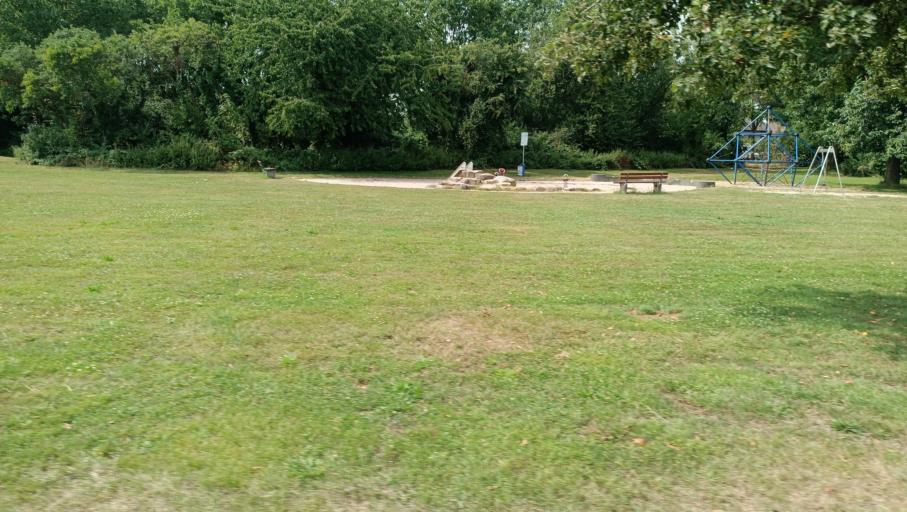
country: DE
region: North Rhine-Westphalia
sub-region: Regierungsbezirk Dusseldorf
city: Moers
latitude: 51.4268
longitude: 6.6850
